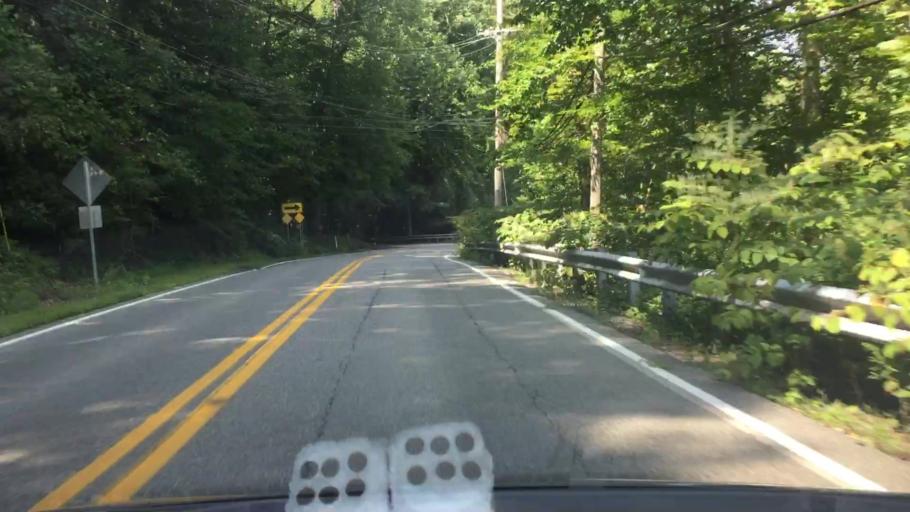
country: US
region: Pennsylvania
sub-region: Delaware County
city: Media
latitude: 39.9051
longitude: -75.3957
